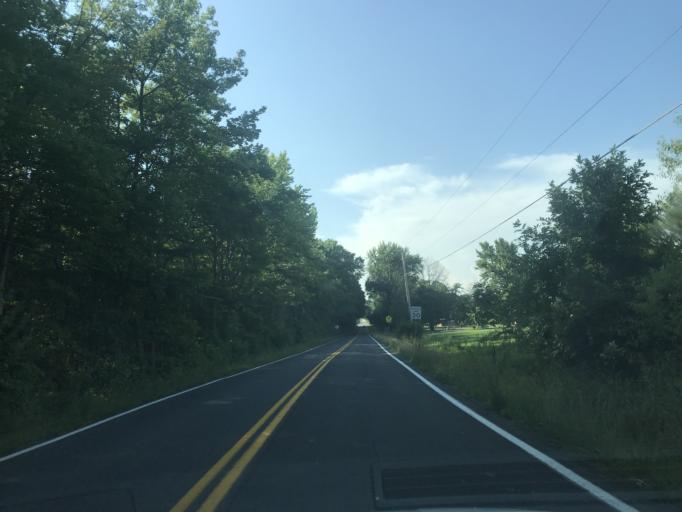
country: US
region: Maryland
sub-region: Harford County
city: Aberdeen
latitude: 39.5191
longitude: -76.1352
